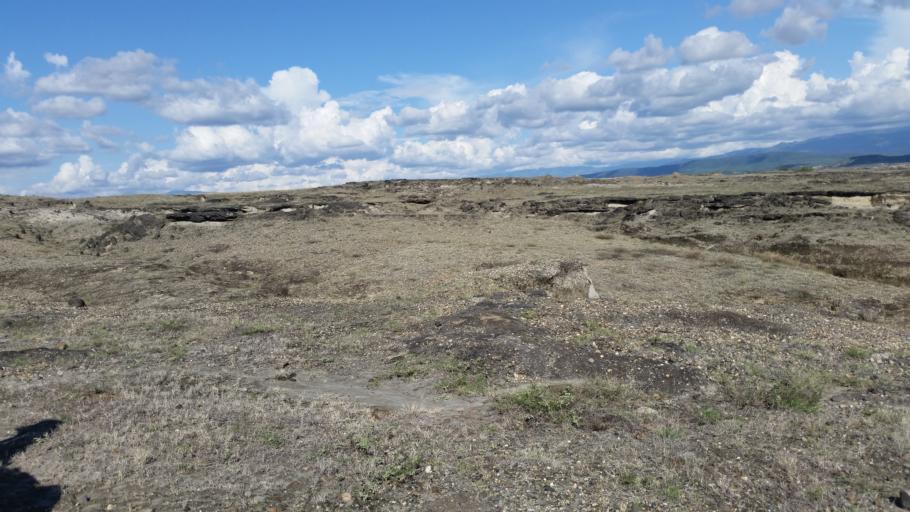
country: CO
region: Huila
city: Villavieja
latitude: 3.2539
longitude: -75.1437
